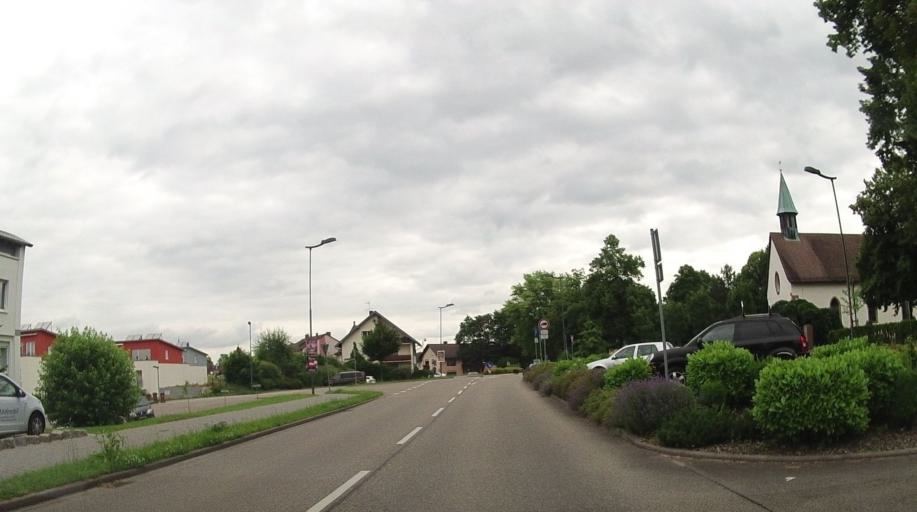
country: DE
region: Baden-Wuerttemberg
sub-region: Karlsruhe Region
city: Kuppenheim
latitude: 48.8230
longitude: 8.2511
